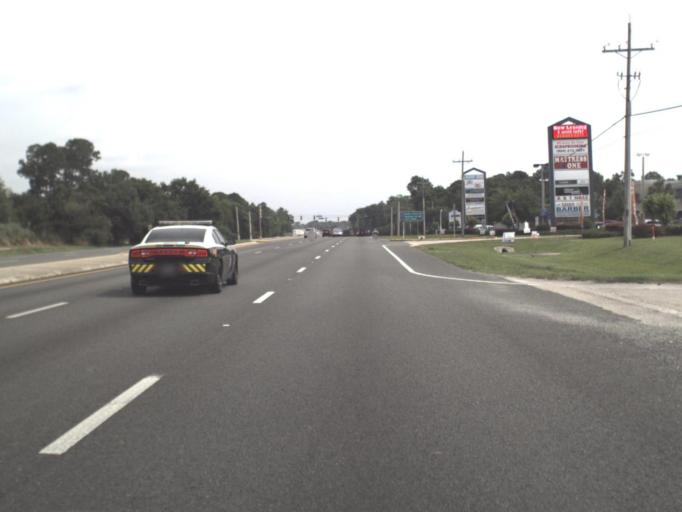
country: US
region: Florida
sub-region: Clay County
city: Orange Park
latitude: 30.1347
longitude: -81.7023
